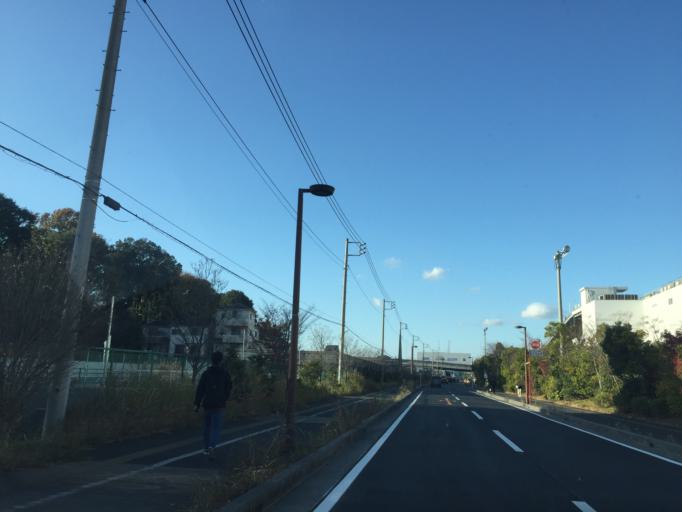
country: JP
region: Saitama
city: Koshigaya
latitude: 35.8902
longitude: 139.7304
